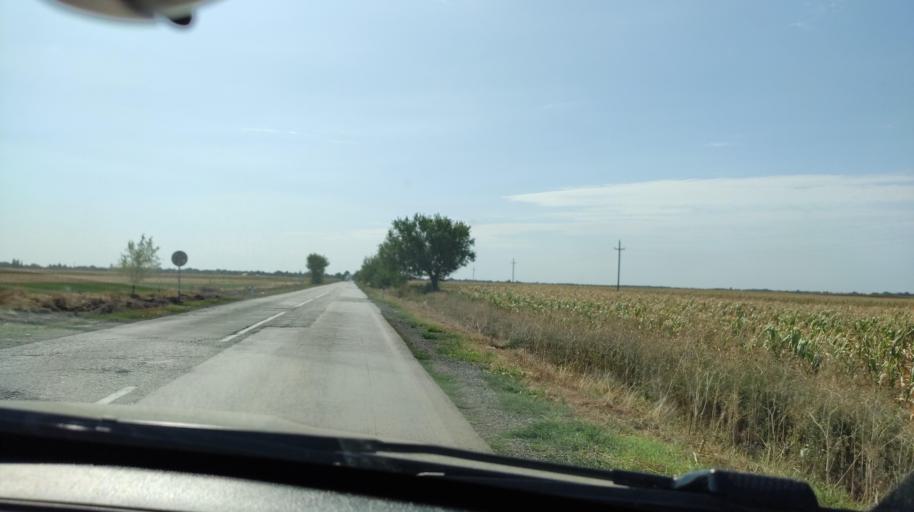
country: RS
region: Autonomna Pokrajina Vojvodina
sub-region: Severnobacki Okrug
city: Backa Topola
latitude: 45.8255
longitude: 19.6013
